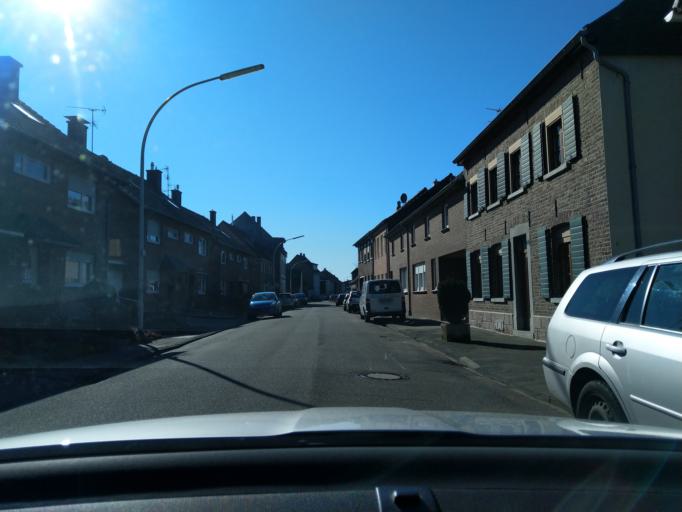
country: DE
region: North Rhine-Westphalia
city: Erkelenz
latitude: 51.1082
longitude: 6.3827
